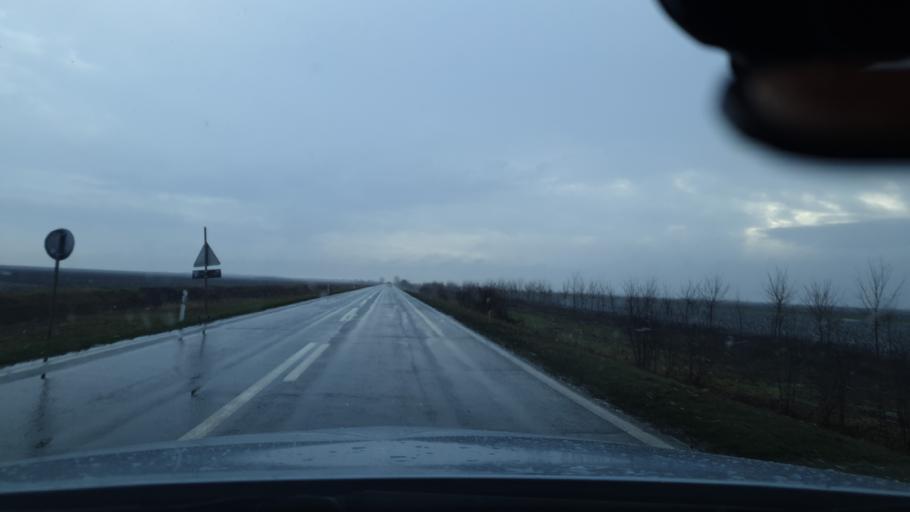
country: RS
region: Autonomna Pokrajina Vojvodina
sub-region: Juznobanatski Okrug
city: Pancevo
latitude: 44.8444
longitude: 20.7889
